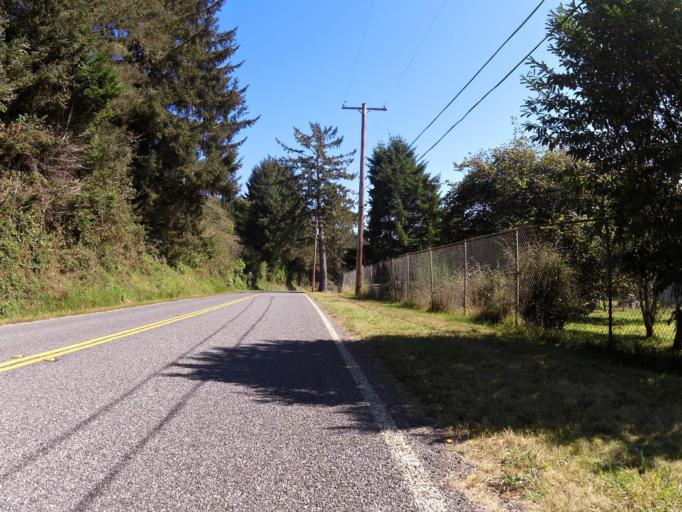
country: US
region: Oregon
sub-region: Curry County
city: Harbor
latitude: 41.9521
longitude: -124.2006
